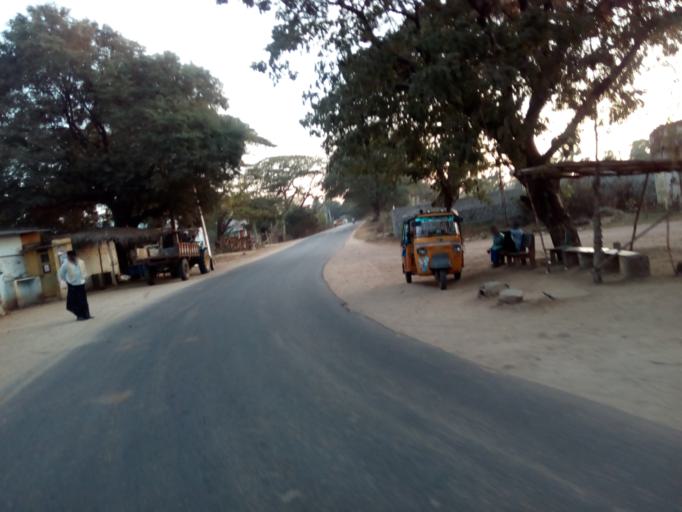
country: IN
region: Andhra Pradesh
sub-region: Prakasam
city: Vetapalem
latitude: 15.7241
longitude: 80.2540
